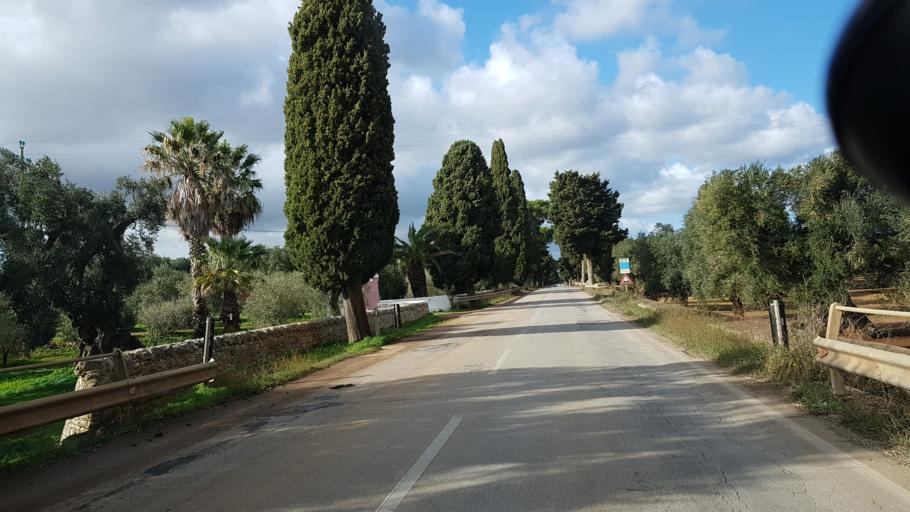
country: IT
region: Apulia
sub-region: Provincia di Brindisi
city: Ostuni
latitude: 40.7542
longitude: 17.5428
